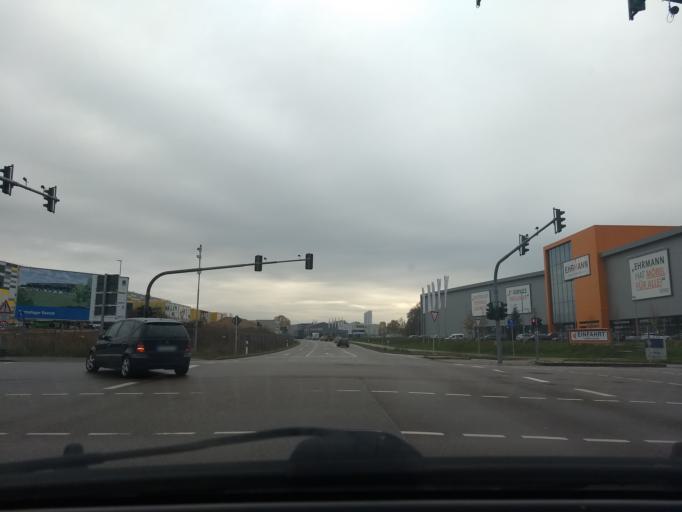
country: DE
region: Baden-Wuerttemberg
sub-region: Karlsruhe Region
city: Rastatt
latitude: 48.8592
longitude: 8.2385
